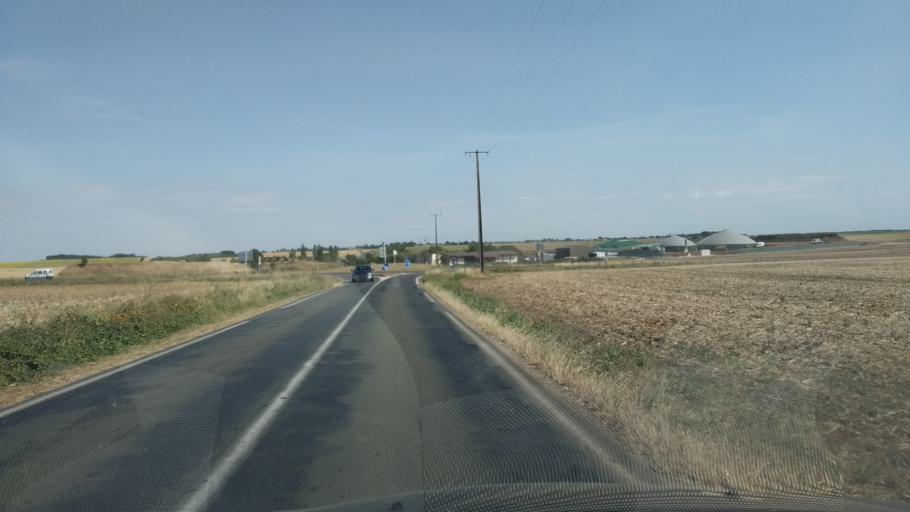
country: FR
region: Poitou-Charentes
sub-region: Departement de la Vienne
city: Cisse
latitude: 46.6653
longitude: 0.2031
